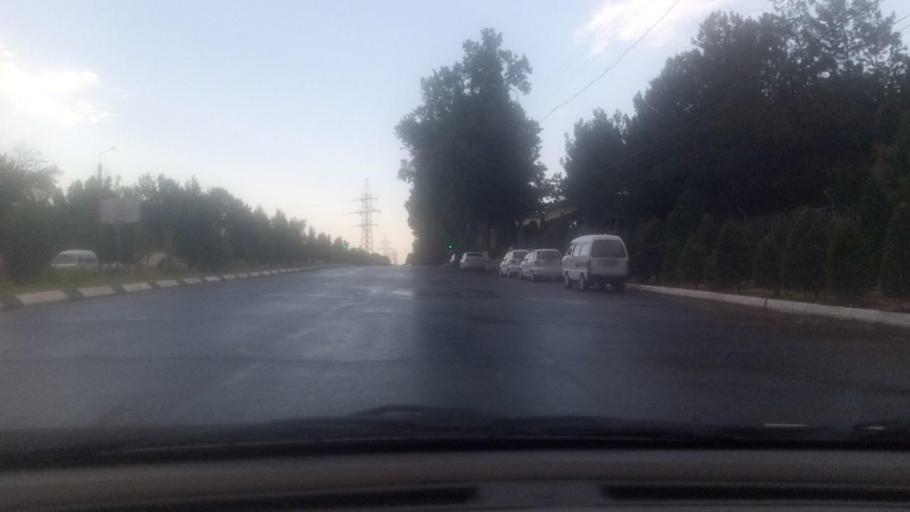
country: UZ
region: Toshkent Shahri
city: Tashkent
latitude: 41.3014
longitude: 69.1937
